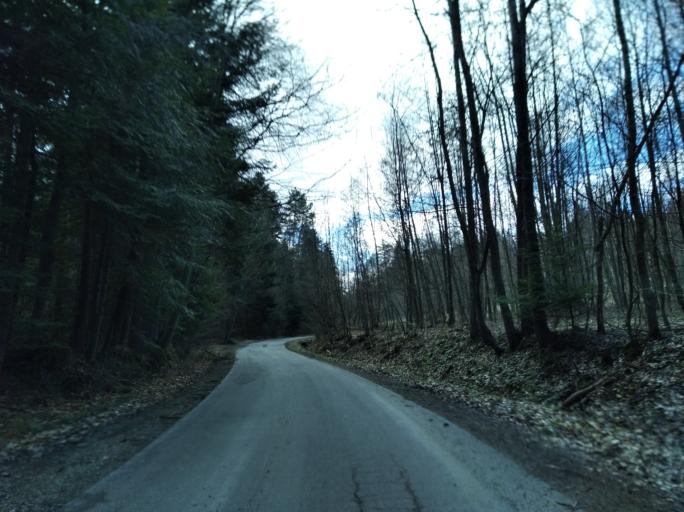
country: PL
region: Subcarpathian Voivodeship
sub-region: Powiat strzyzowski
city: Wysoka Strzyzowska
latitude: 49.8005
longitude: 21.7370
